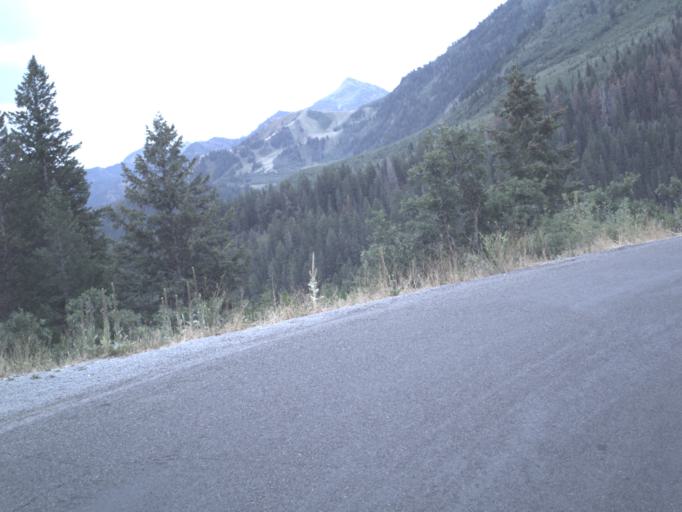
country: US
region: Utah
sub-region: Utah County
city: Lindon
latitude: 40.4082
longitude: -111.6030
